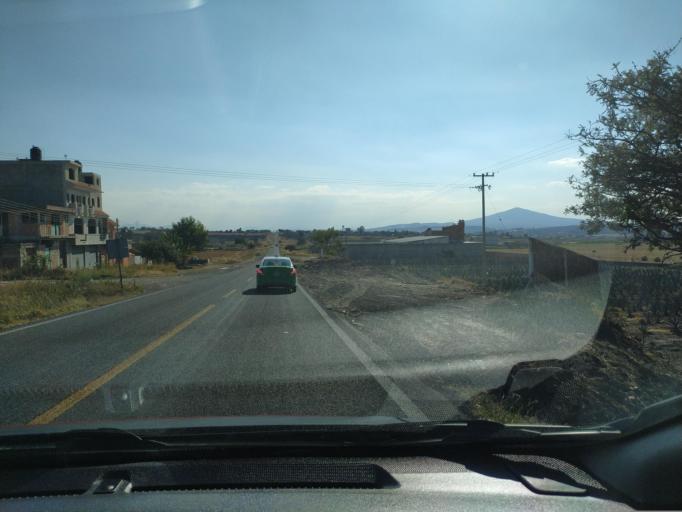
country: MX
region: Guanajuato
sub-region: Penjamo
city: Estacion la Piedad
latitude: 20.4200
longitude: -101.9932
